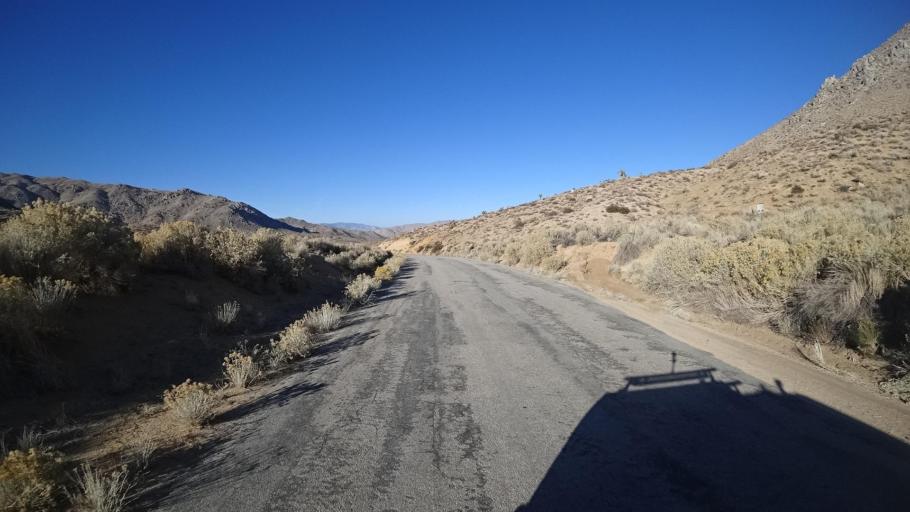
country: US
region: California
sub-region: Kern County
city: Weldon
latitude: 35.4694
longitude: -118.2112
